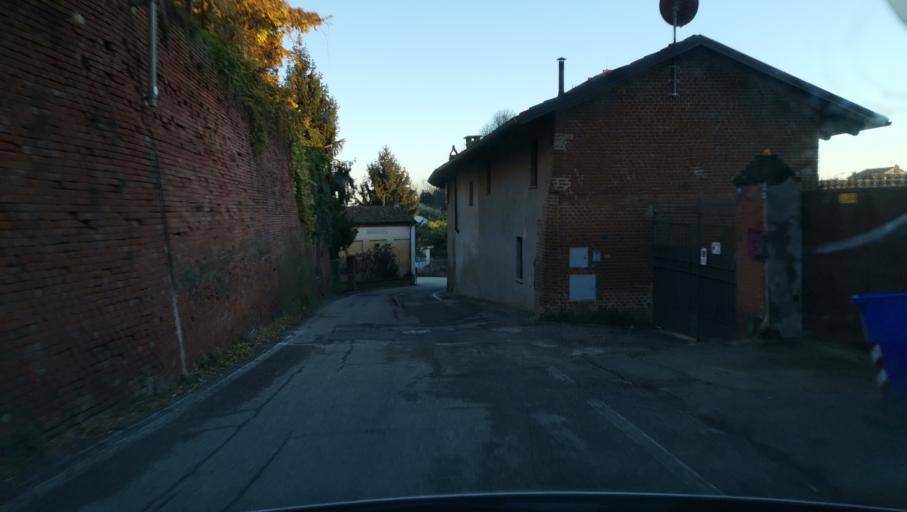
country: IT
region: Piedmont
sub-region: Provincia di Asti
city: Moncucco Torinese
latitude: 45.0693
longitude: 7.9319
